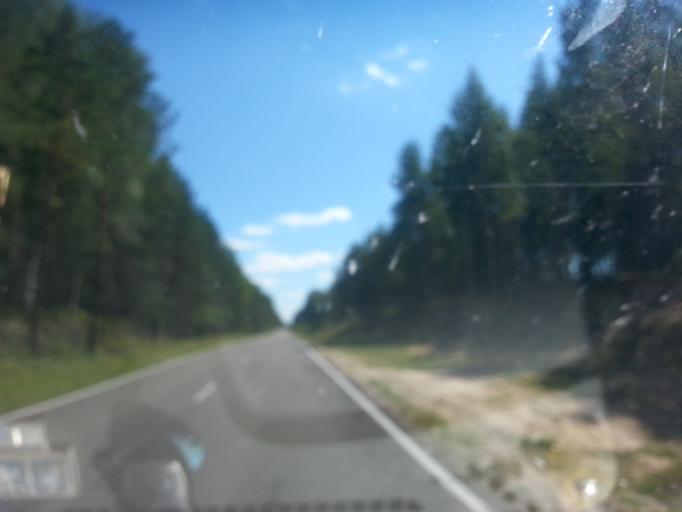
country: RU
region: Vladimir
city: Galitsy
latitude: 56.0727
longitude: 42.8671
